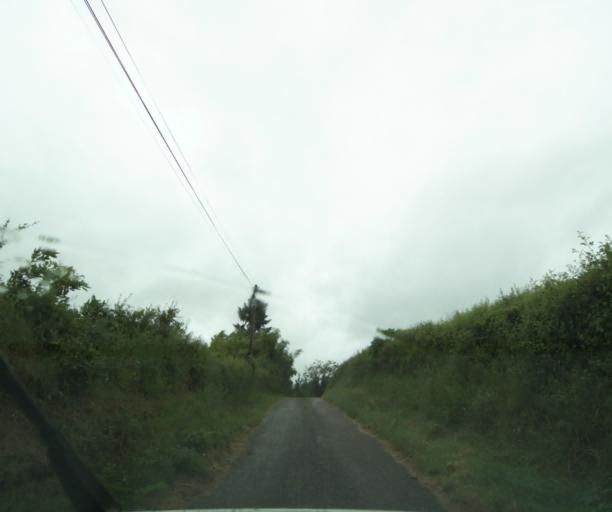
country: FR
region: Bourgogne
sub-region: Departement de Saone-et-Loire
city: Saint-Vallier
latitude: 46.4930
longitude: 4.4641
